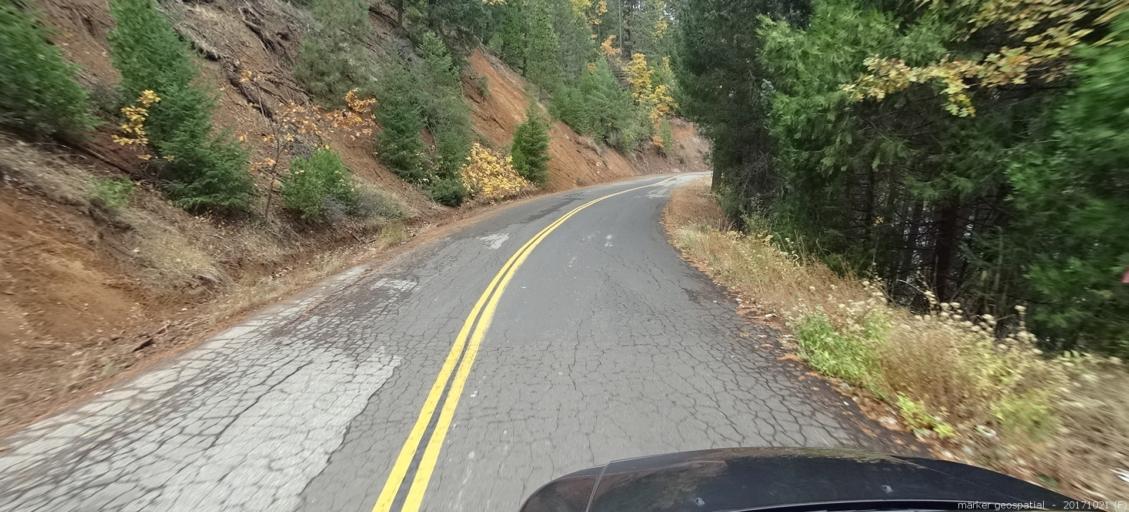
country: US
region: California
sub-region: Shasta County
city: Burney
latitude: 41.0203
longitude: -121.6704
